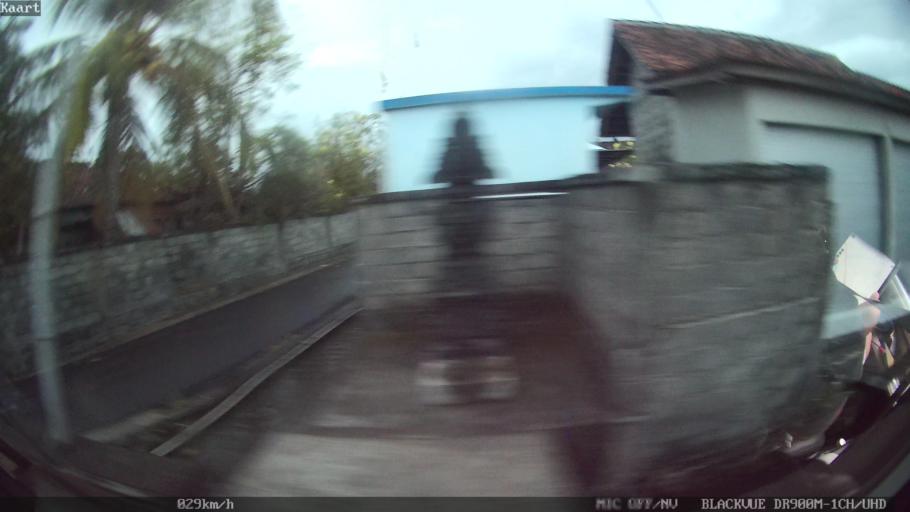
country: ID
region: Bali
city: Banjar Pasekan
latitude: -8.6141
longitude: 115.2851
